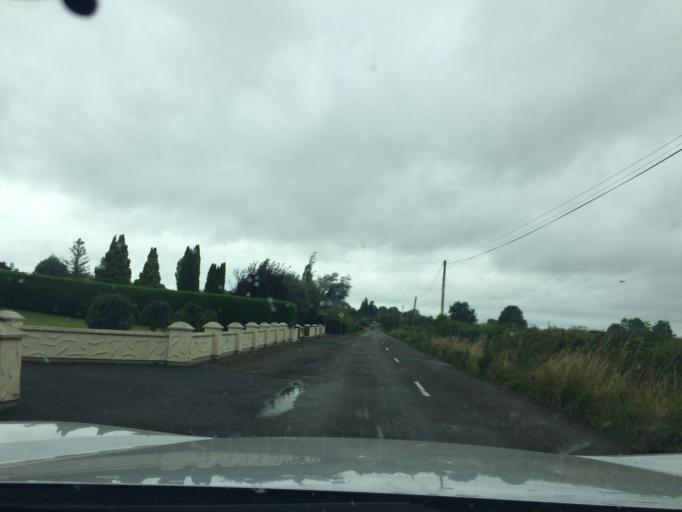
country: IE
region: Munster
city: Thurles
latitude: 52.6189
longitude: -7.8800
